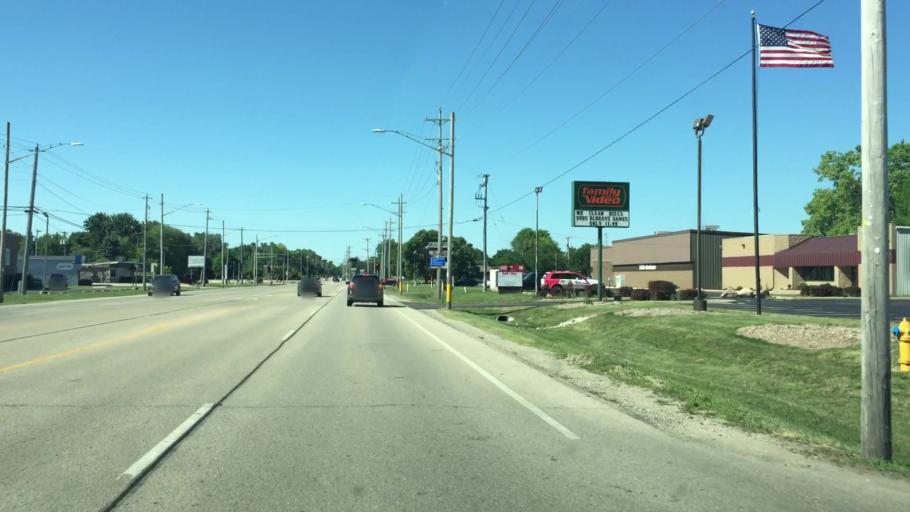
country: US
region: Wisconsin
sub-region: Winnebago County
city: Menasha
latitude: 44.2240
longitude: -88.4262
